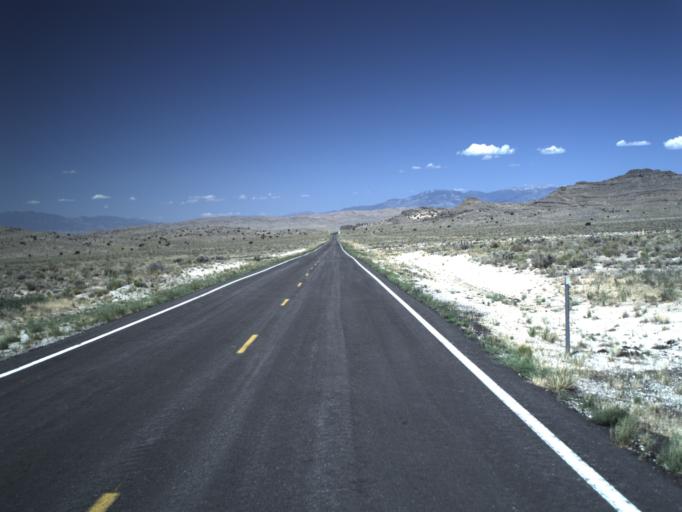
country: US
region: Utah
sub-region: Beaver County
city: Milford
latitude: 39.0754
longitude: -113.6786
